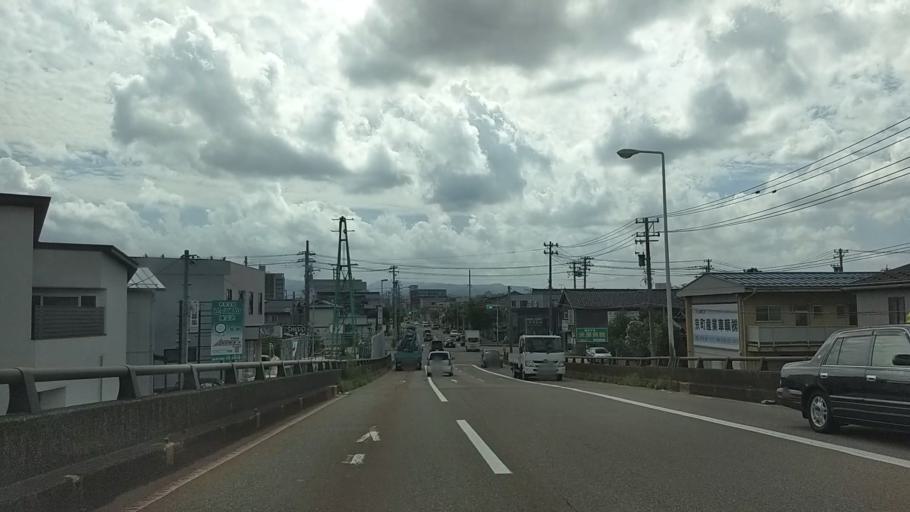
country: JP
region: Ishikawa
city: Kanazawa-shi
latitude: 36.5869
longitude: 136.6633
